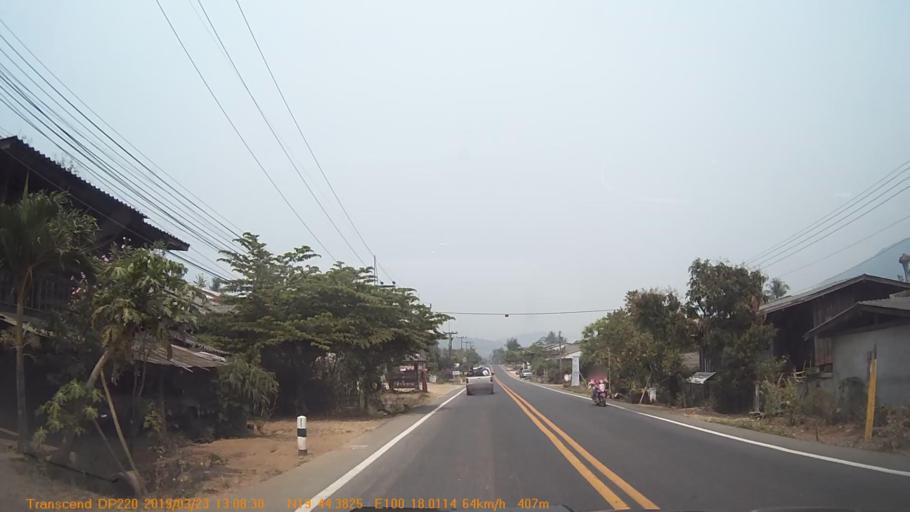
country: TH
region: Chiang Rai
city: Khun Tan
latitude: 19.7400
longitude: 100.3002
